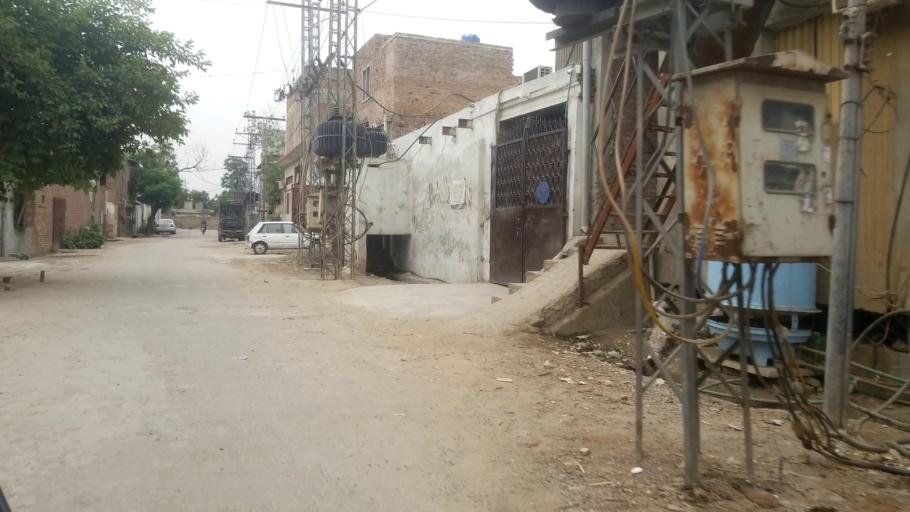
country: PK
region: Khyber Pakhtunkhwa
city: Peshawar
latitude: 33.9807
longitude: 71.5581
